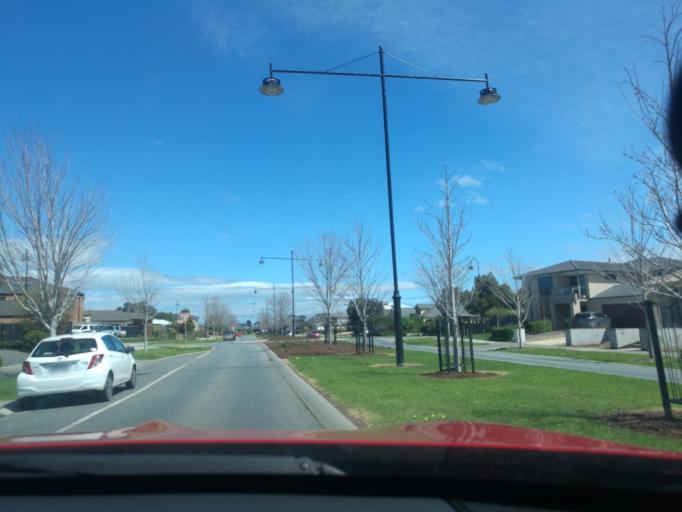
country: AU
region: Victoria
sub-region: Casey
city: Lynbrook
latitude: -38.0741
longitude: 145.2458
